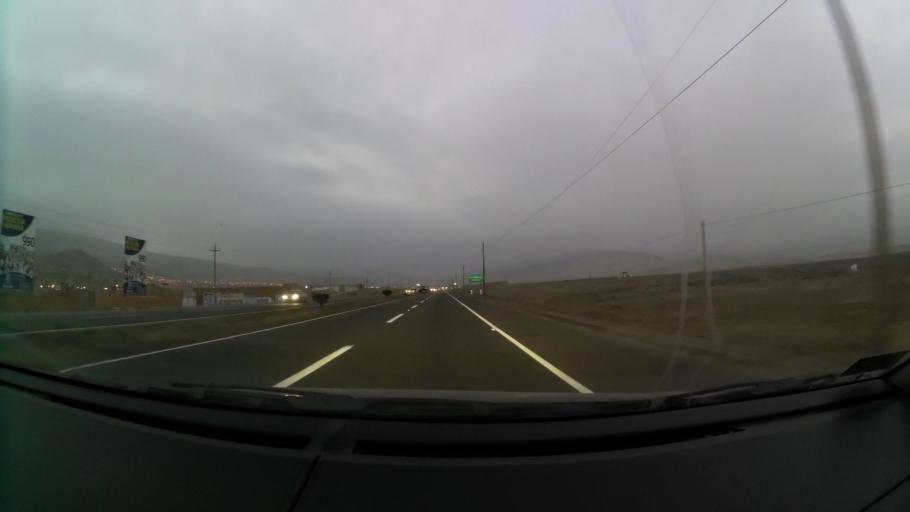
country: PE
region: Lima
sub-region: Lima
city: Santa Rosa
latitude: -11.7520
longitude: -77.1476
